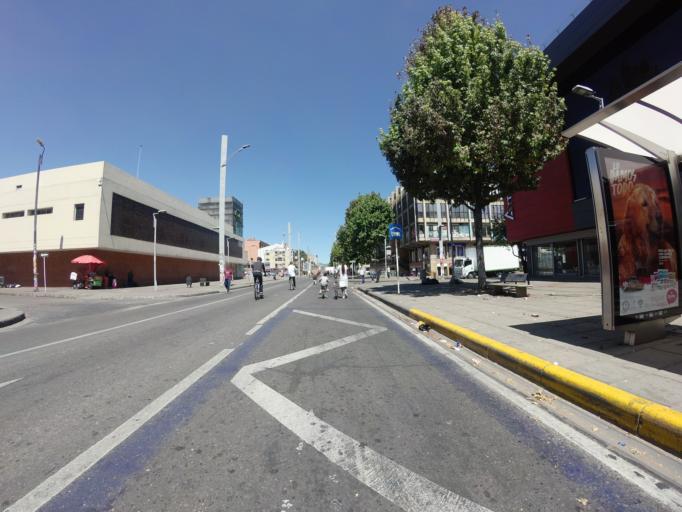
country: CO
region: Bogota D.C.
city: Barrio San Luis
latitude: 4.6694
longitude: -74.0556
